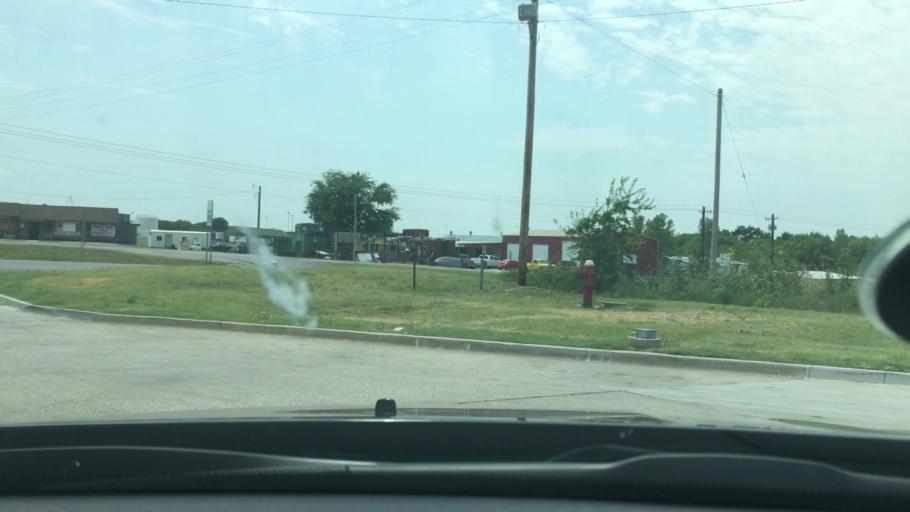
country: US
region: Oklahoma
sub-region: Love County
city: Marietta
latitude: 33.9409
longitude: -97.1380
